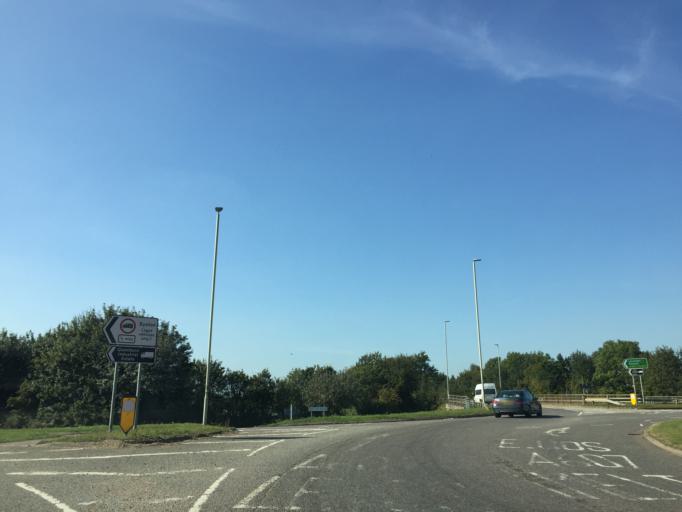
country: GB
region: England
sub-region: Leicestershire
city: Queniborough
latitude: 52.7095
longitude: -1.0507
